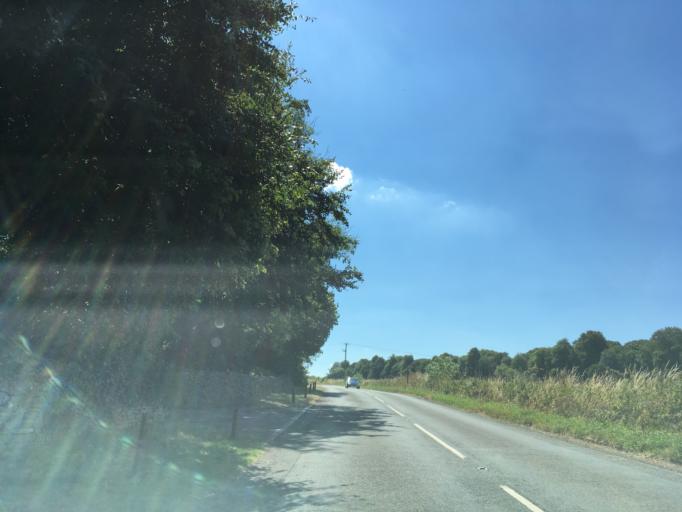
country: GB
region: England
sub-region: South Gloucestershire
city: Hinton
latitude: 51.5081
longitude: -2.3413
